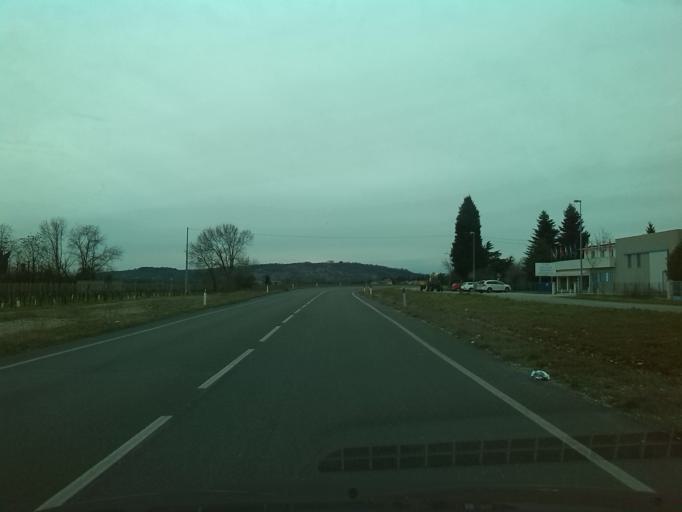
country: IT
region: Friuli Venezia Giulia
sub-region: Provincia di Gorizia
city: Mariano del Friuli
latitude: 45.9045
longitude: 13.4649
